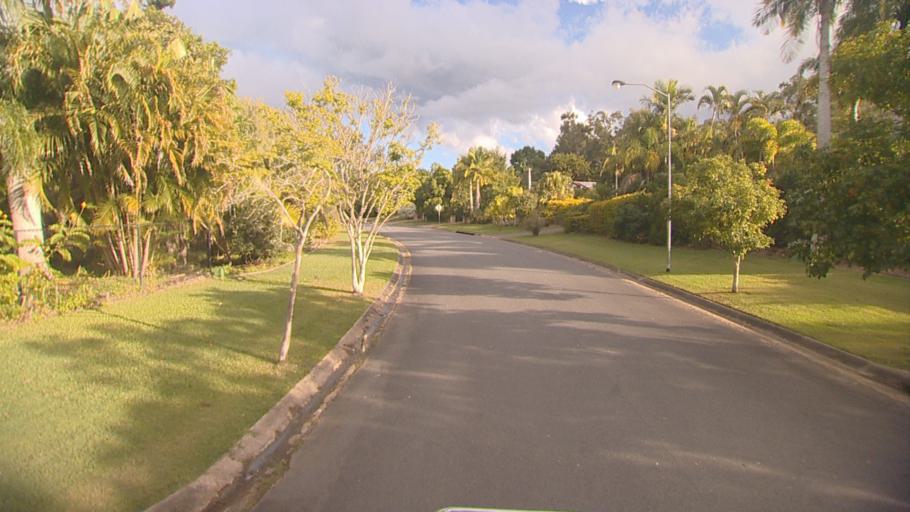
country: AU
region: Queensland
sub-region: Logan
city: Park Ridge South
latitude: -27.7038
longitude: 153.0243
